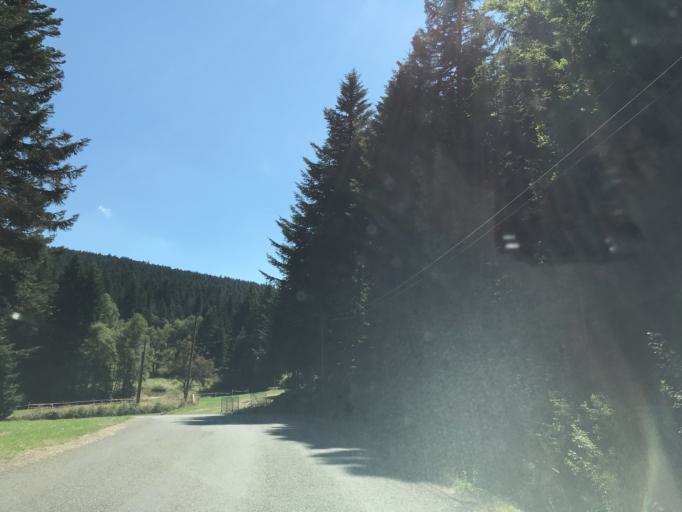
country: FR
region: Rhone-Alpes
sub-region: Departement de la Loire
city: Noiretable
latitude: 45.7894
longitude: 3.7173
